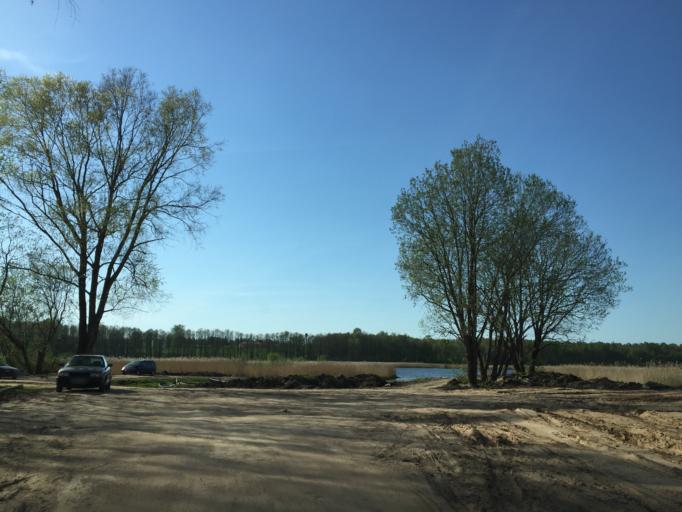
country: LV
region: Limbazu Rajons
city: Limbazi
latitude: 57.5196
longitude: 24.7035
